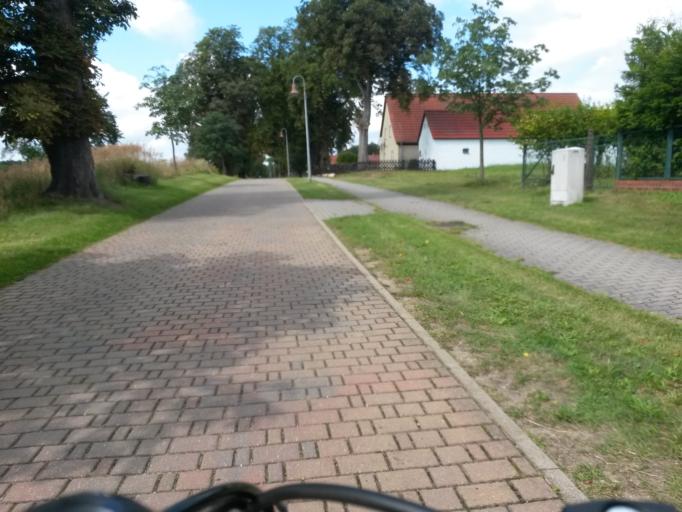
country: DE
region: Brandenburg
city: Angermunde
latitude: 53.0251
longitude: 13.8957
